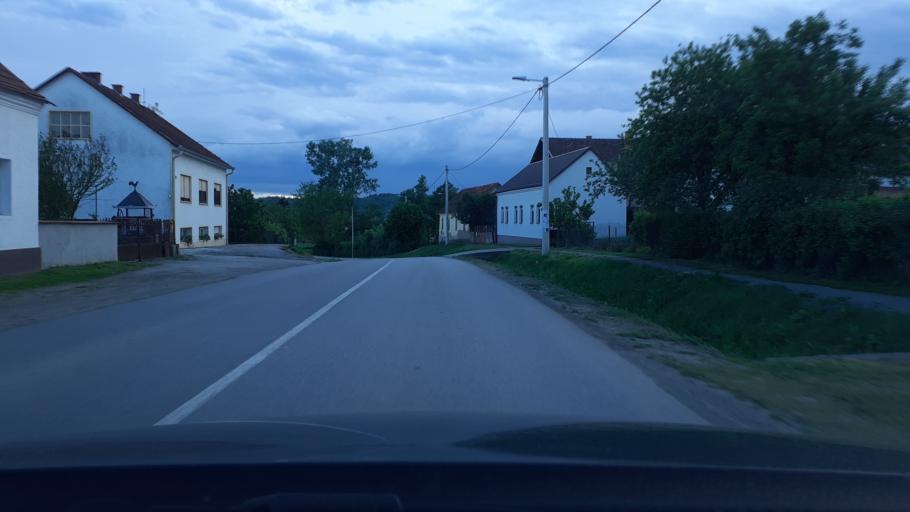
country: HR
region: Pozesko-Slavonska
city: Gradac
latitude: 45.3089
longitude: 17.8102
